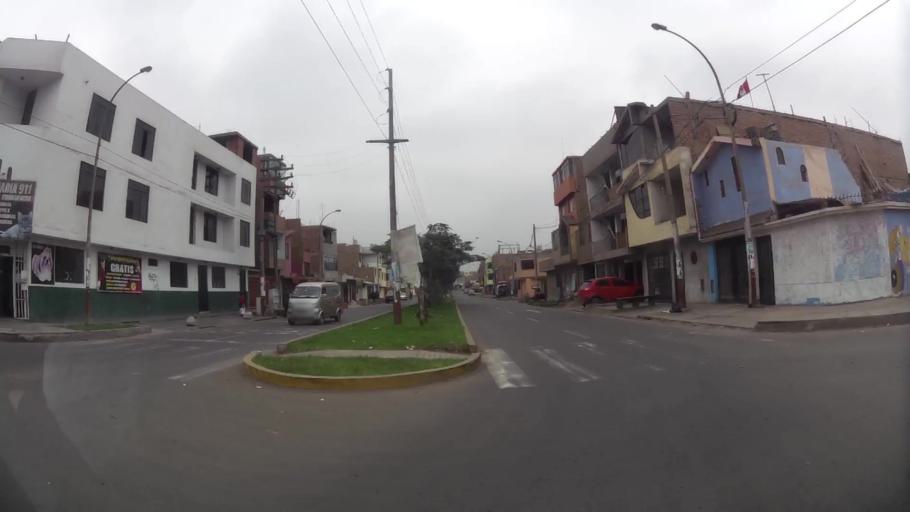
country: PE
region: Lima
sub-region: Lima
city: Independencia
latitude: -11.9434
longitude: -77.0893
